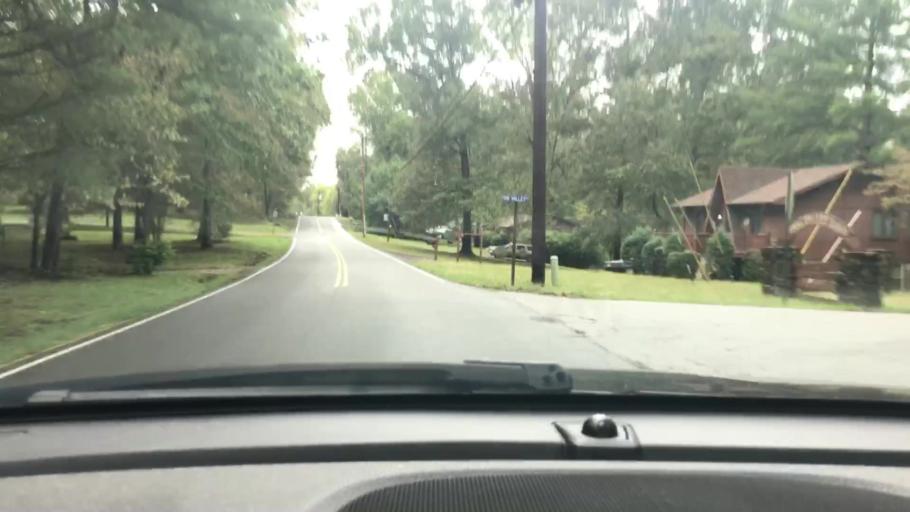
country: US
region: Tennessee
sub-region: Cheatham County
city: Kingston Springs
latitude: 36.1073
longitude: -87.1372
